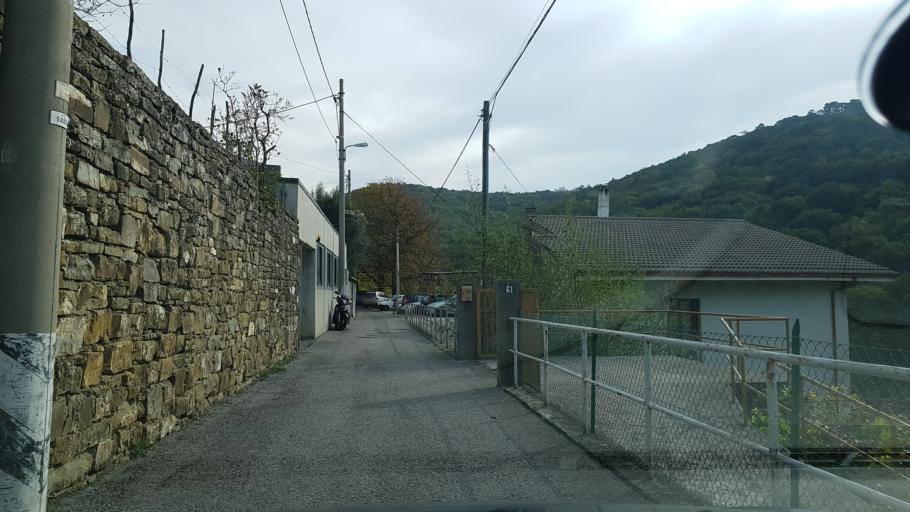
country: IT
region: Friuli Venezia Giulia
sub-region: Provincia di Trieste
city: Trieste
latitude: 45.6501
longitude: 13.8106
